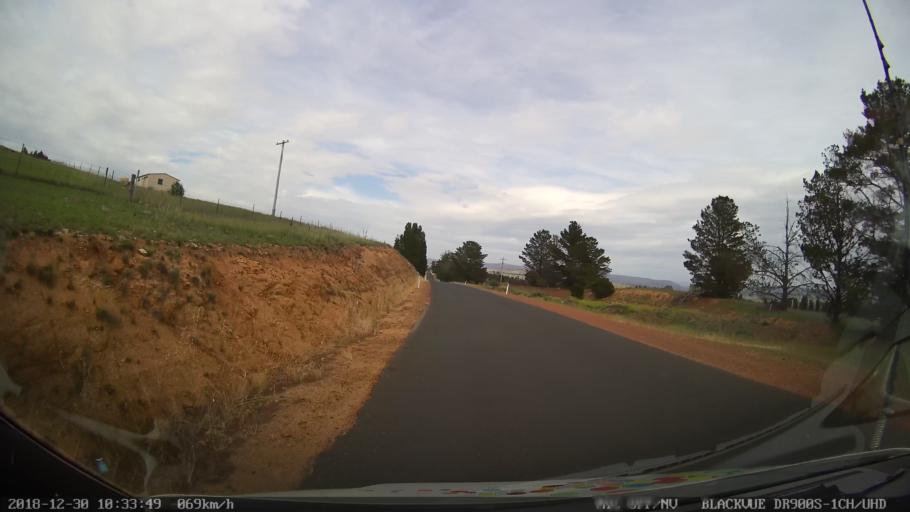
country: AU
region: New South Wales
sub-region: Snowy River
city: Berridale
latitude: -36.4986
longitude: 148.8482
